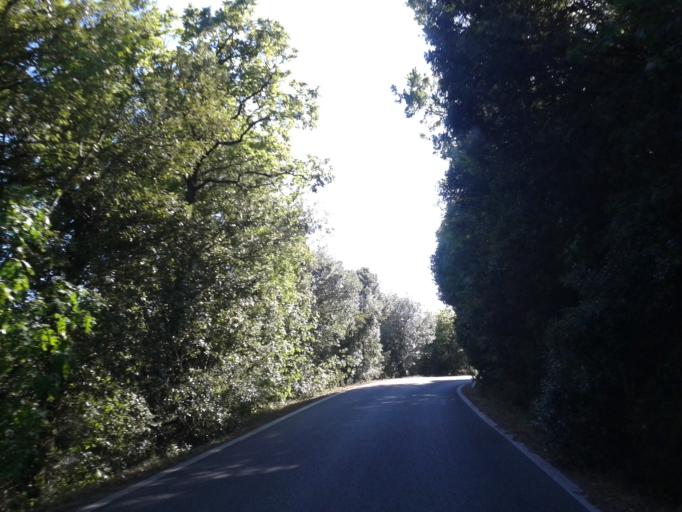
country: IT
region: Tuscany
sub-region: Province of Pisa
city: Castellina Marittima
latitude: 43.4330
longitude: 10.6144
